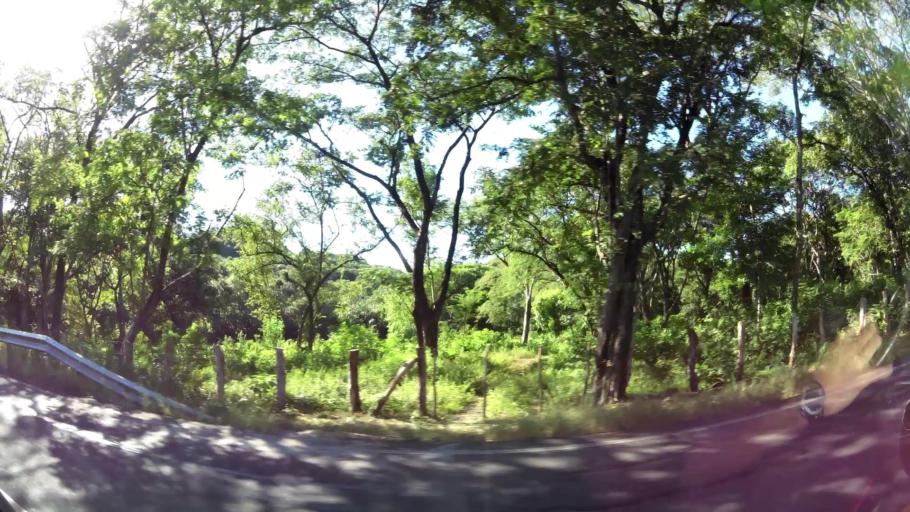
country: CR
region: Guanacaste
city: Belen
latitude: 10.3631
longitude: -85.6601
